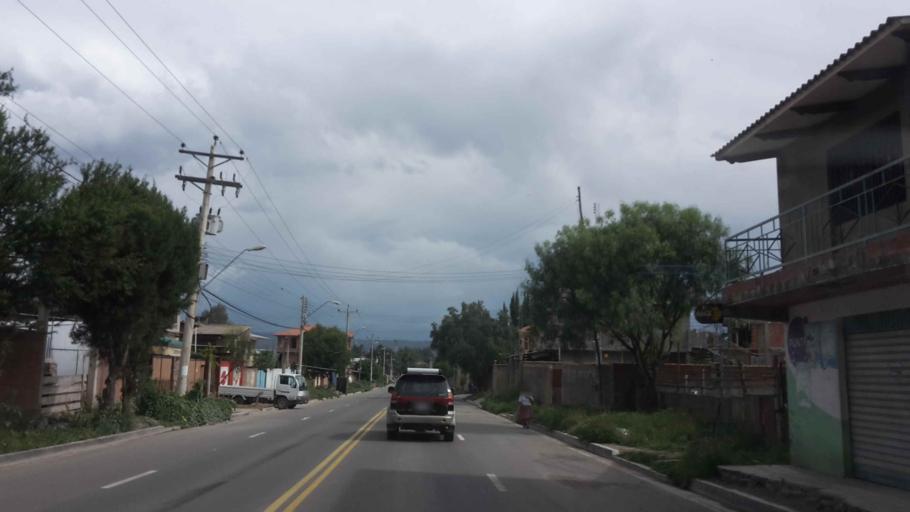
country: BO
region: Cochabamba
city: Cochabamba
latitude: -17.3703
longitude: -66.2524
